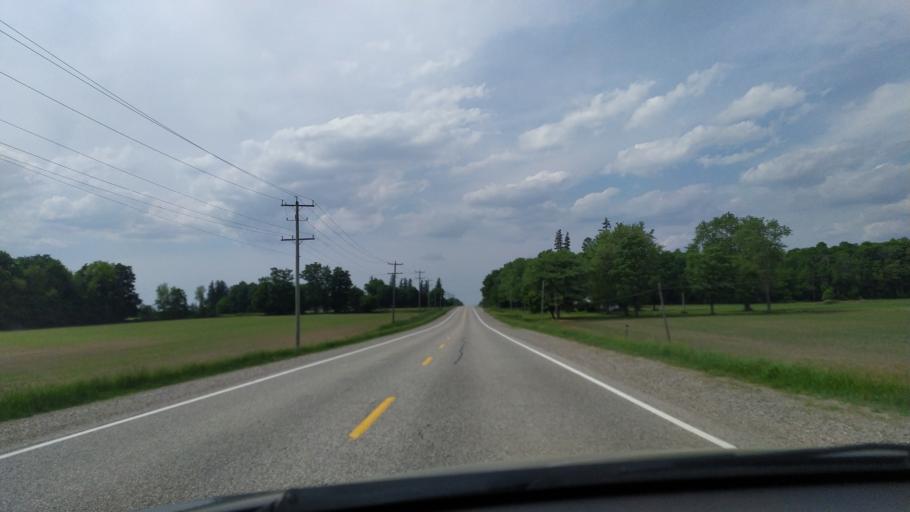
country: CA
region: Ontario
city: Dorchester
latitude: 43.0945
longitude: -81.0074
